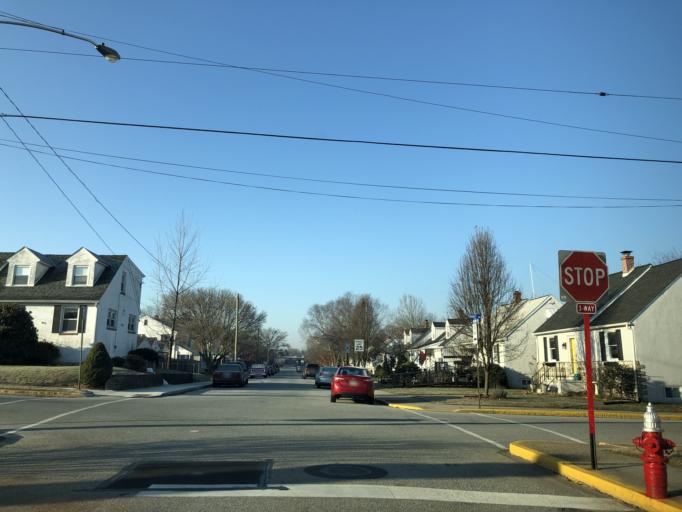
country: US
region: Pennsylvania
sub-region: Chester County
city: Downingtown
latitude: 40.0038
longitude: -75.7152
